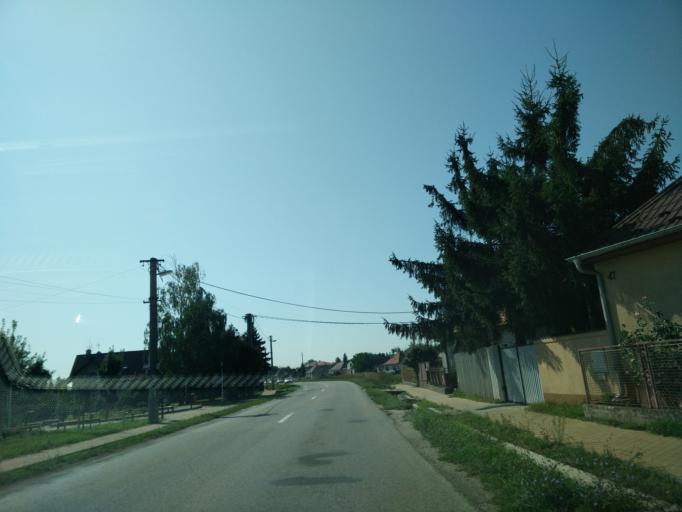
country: SK
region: Nitriansky
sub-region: Okres Nitra
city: Nitra
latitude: 48.3624
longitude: 18.0210
